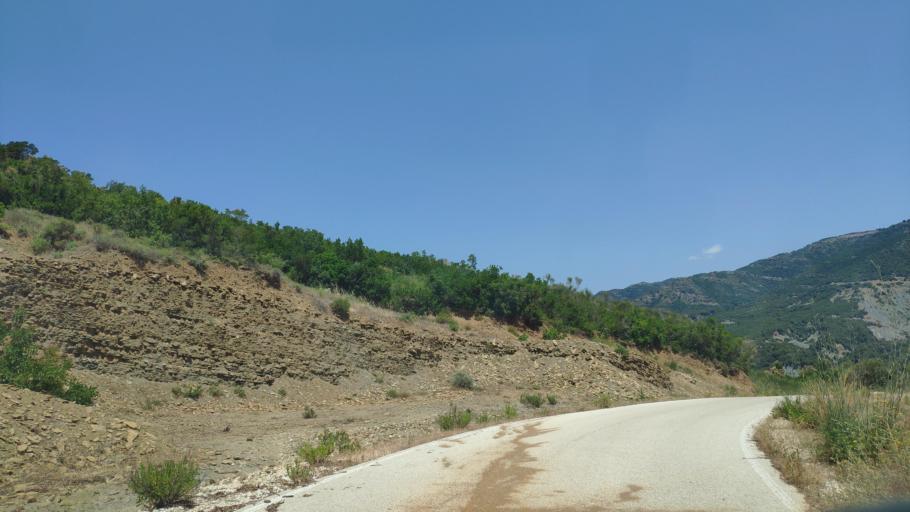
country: GR
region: West Greece
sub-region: Nomos Aitolias kai Akarnanias
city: Sardinia
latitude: 38.8836
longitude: 21.2793
